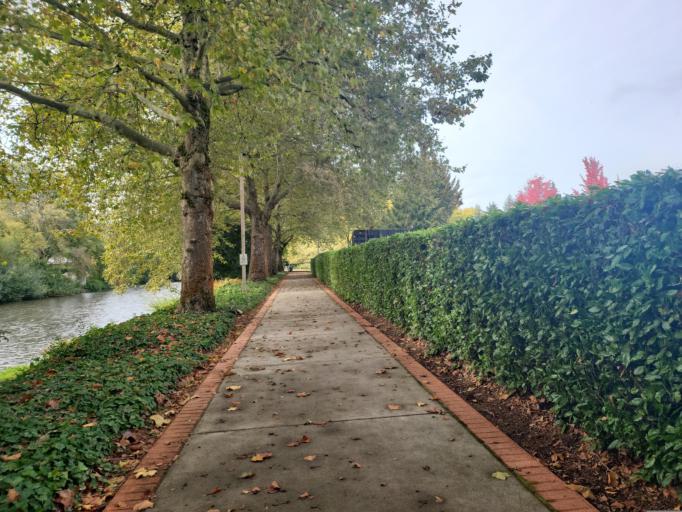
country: US
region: Washington
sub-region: King County
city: Renton
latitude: 47.4850
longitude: -122.2071
